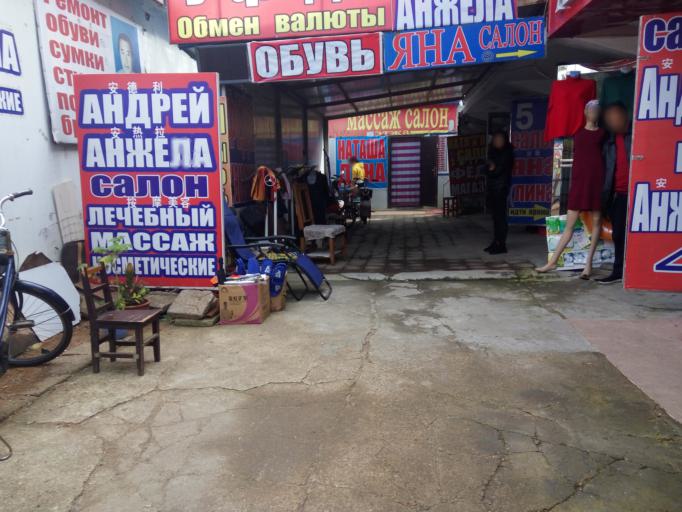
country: CN
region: Heilongjiang Sheng
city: Erjing
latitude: 48.6491
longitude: 126.1430
